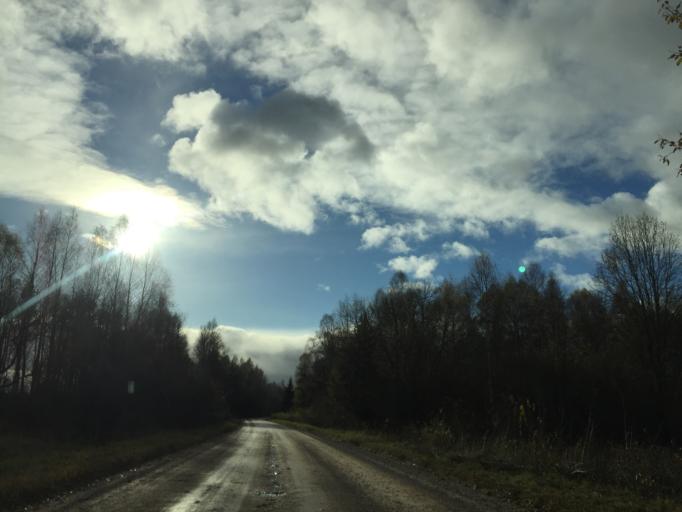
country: LV
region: Tukuma Rajons
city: Tukums
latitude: 56.9793
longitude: 22.9805
